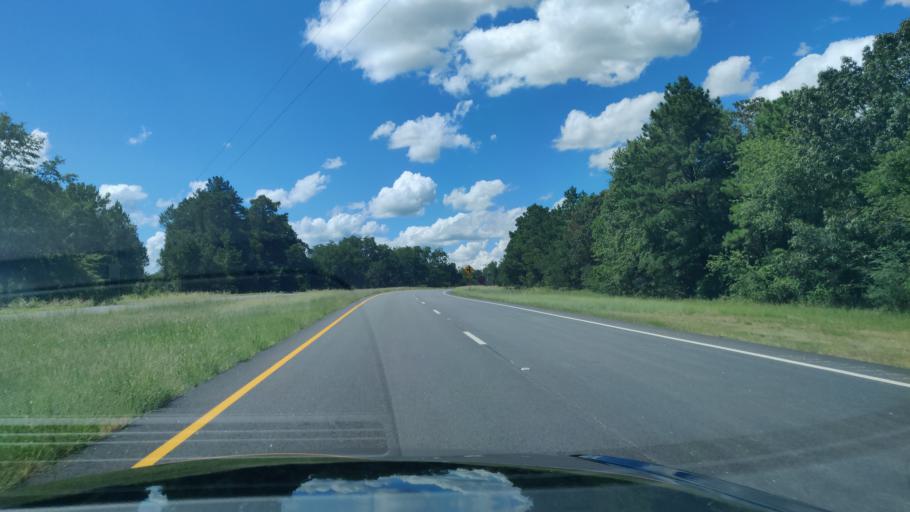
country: US
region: Georgia
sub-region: Stewart County
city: Richland
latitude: 32.1085
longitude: -84.6753
